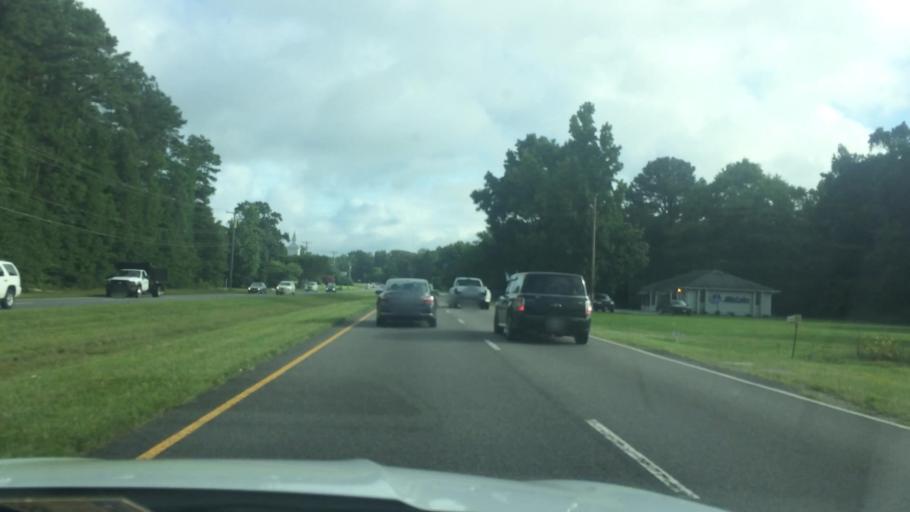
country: US
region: Virginia
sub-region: Gloucester County
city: Gloucester Point
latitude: 37.3275
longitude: -76.5144
